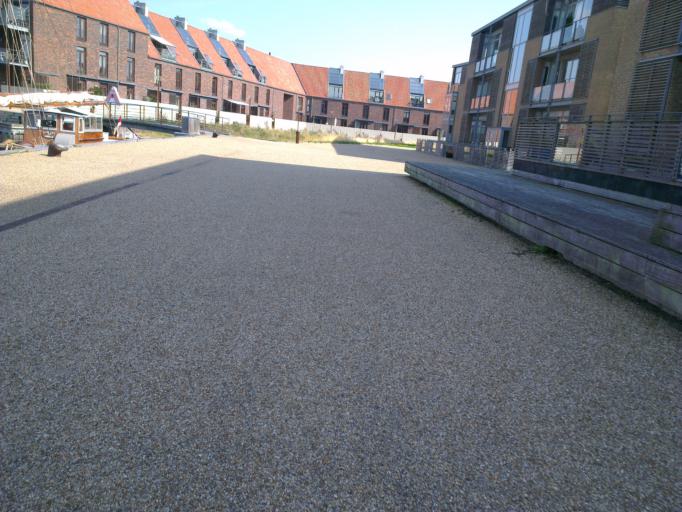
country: DK
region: Capital Region
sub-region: Frederikssund Kommune
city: Frederikssund
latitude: 55.8352
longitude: 12.0555
